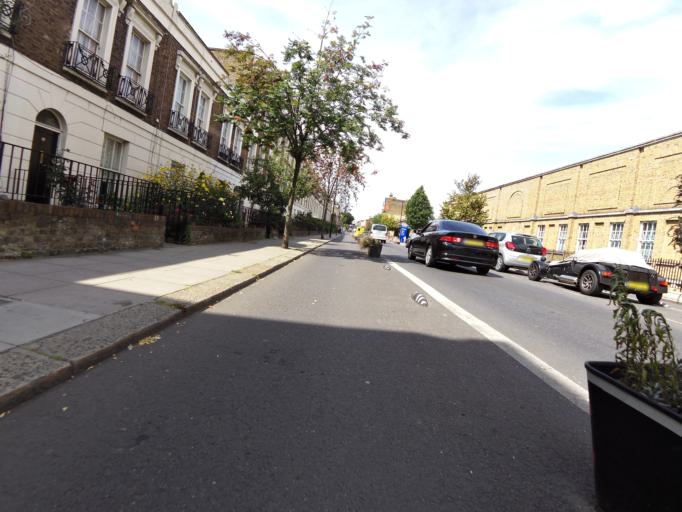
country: GB
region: England
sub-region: Greater London
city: Camden Town
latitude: 51.5380
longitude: -0.1353
